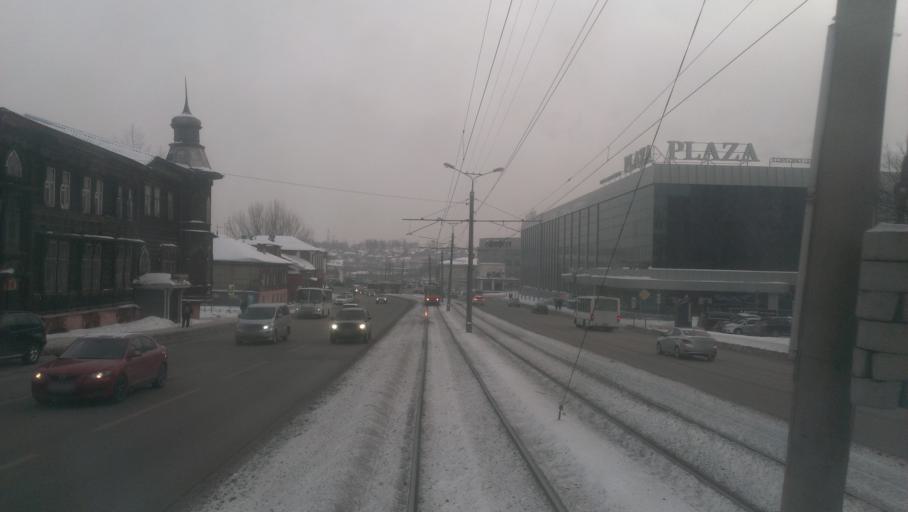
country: RU
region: Altai Krai
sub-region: Gorod Barnaulskiy
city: Barnaul
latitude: 53.3318
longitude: 83.7812
